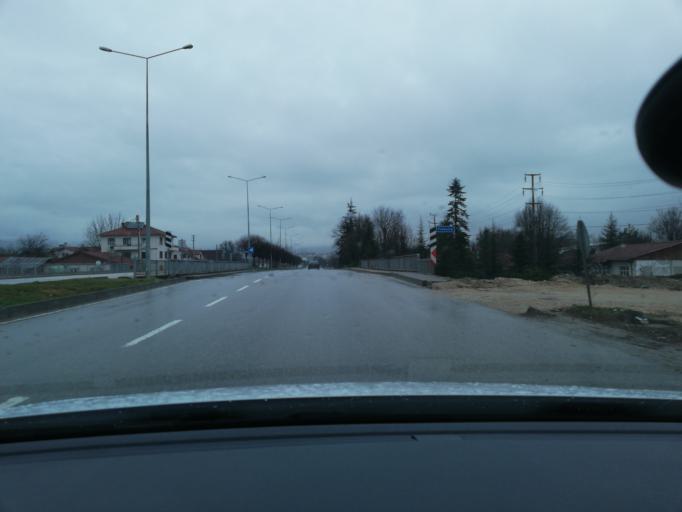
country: TR
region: Bolu
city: Bolu
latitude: 40.7116
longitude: 31.6160
